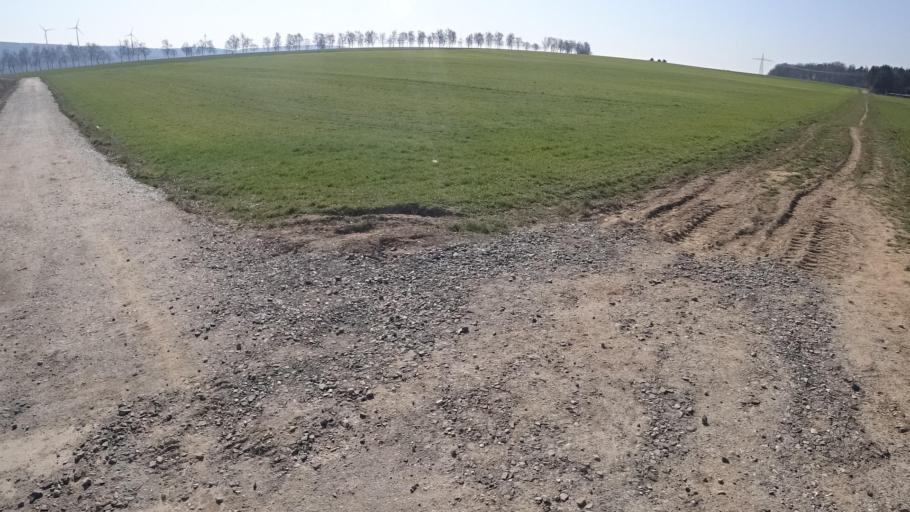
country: DE
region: Rheinland-Pfalz
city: Rheinbollen
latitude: 50.0071
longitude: 7.6587
